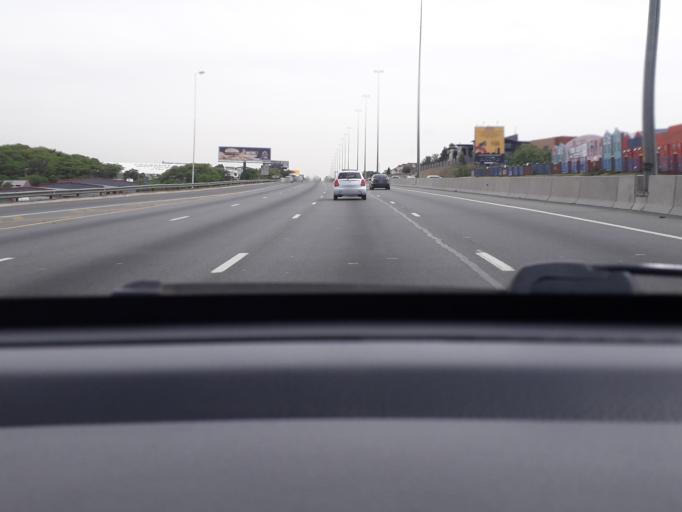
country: ZA
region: Gauteng
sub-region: City of Johannesburg Metropolitan Municipality
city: Roodepoort
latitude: -26.0770
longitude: 27.9715
